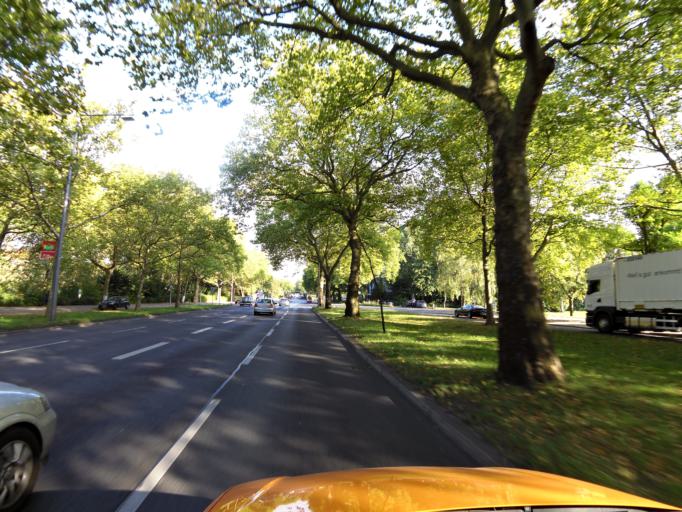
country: DE
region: Berlin
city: Wilhelmstadt
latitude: 52.5137
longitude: 13.1938
